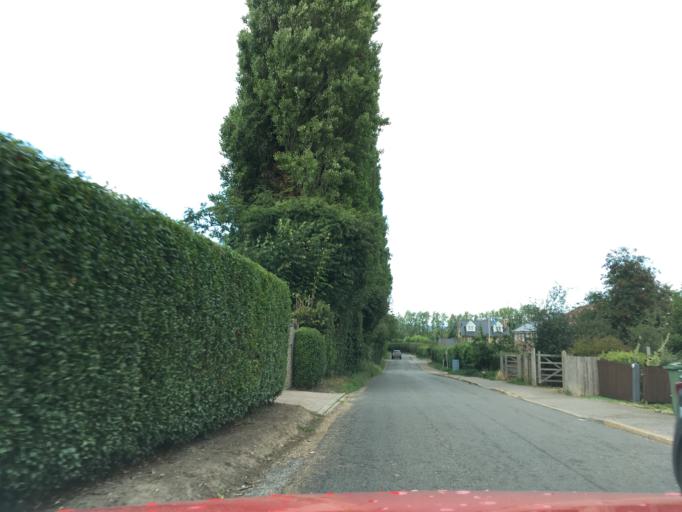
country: GB
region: England
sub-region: Kent
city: Maidstone
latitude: 51.2330
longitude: 0.5215
